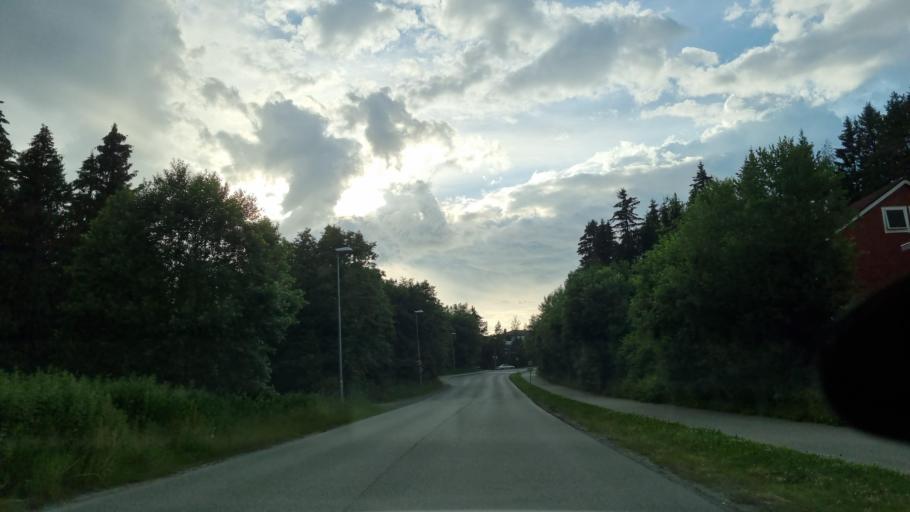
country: NO
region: Sor-Trondelag
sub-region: Trondheim
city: Trondheim
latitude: 63.3829
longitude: 10.3299
